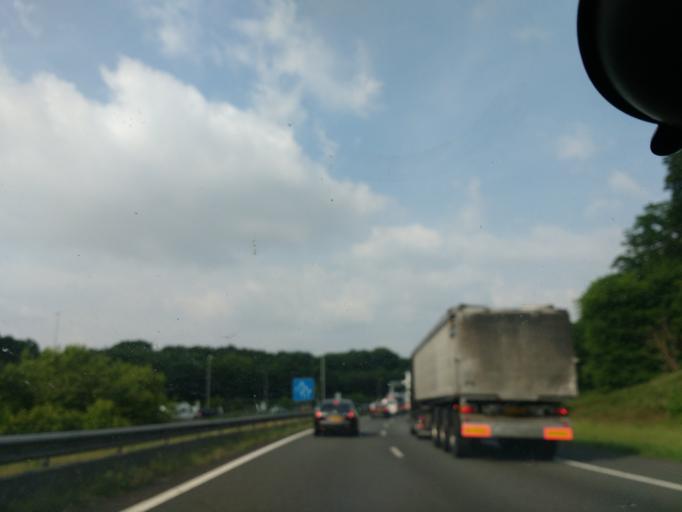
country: NL
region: Gelderland
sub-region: Gemeente Renkum
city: Wolfheze
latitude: 52.0252
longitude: 5.8237
